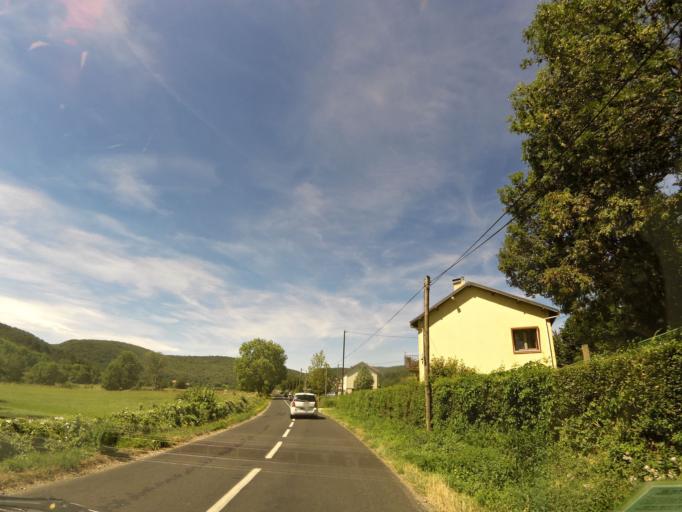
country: FR
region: Midi-Pyrenees
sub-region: Departement de l'Aveyron
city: La Cavalerie
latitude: 43.9744
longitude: 3.3655
